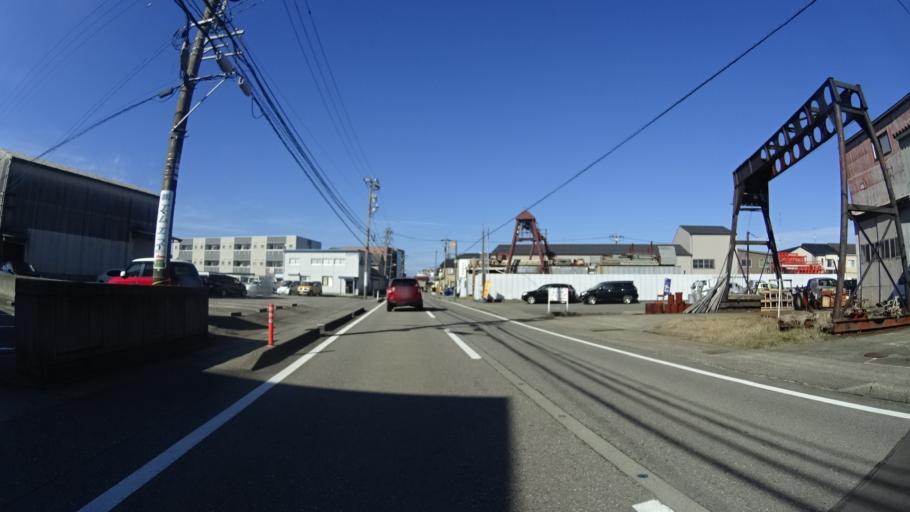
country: JP
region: Ishikawa
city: Kanazawa-shi
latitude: 36.6003
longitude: 136.6081
